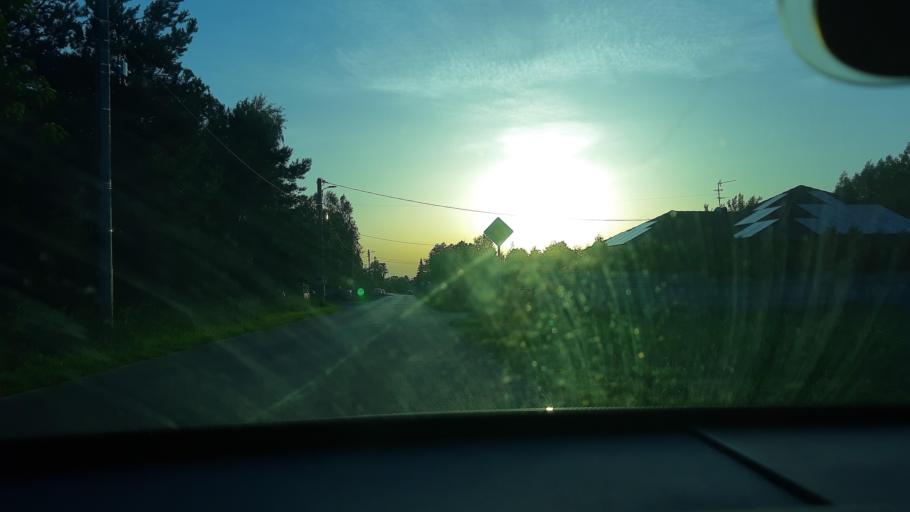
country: PL
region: Lodz Voivodeship
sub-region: Powiat zdunskowolski
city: Zdunska Wola
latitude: 51.6102
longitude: 18.9721
